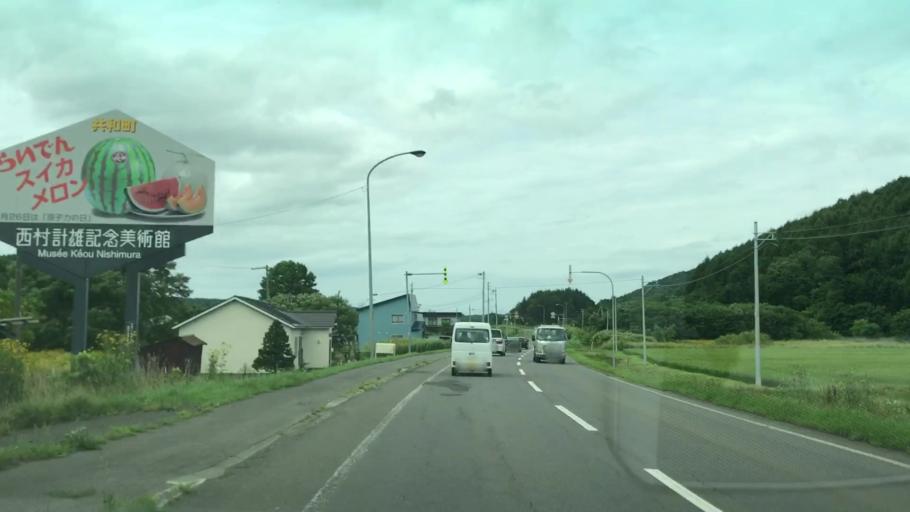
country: JP
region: Hokkaido
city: Iwanai
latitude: 42.9673
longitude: 140.6855
